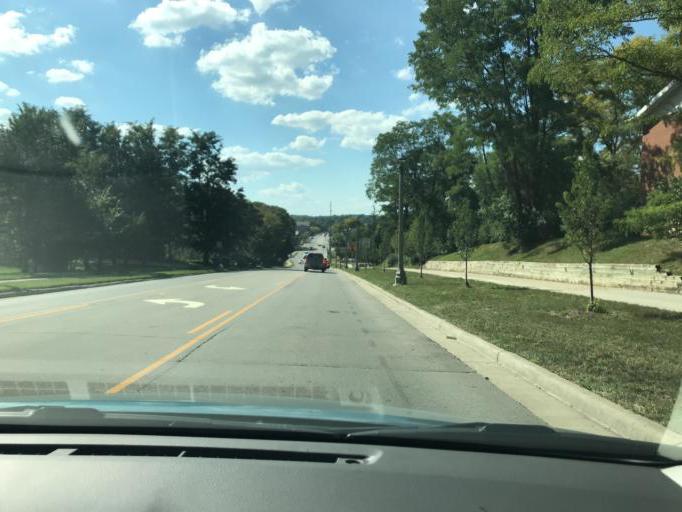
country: US
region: Wisconsin
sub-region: Walworth County
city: Lake Geneva
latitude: 42.5917
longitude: -88.4272
